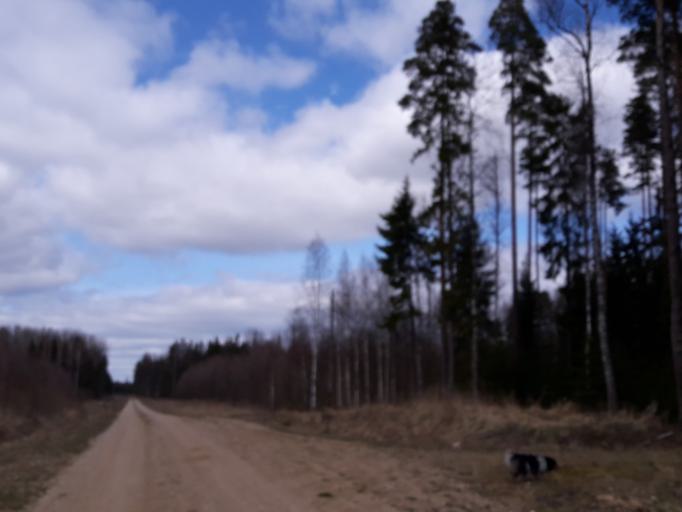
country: LV
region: Talsu Rajons
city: Sabile
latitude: 56.8993
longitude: 22.3778
